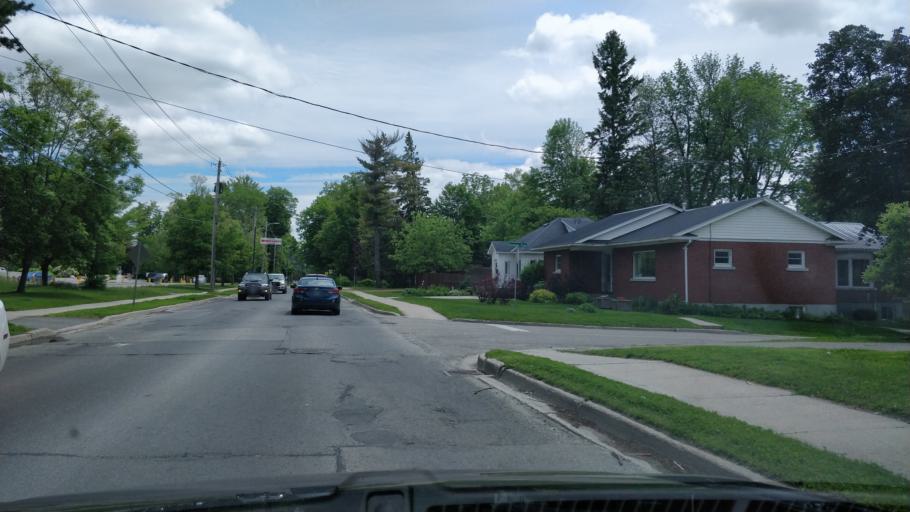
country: CA
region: Ontario
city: Perth
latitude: 44.9067
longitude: -76.2551
